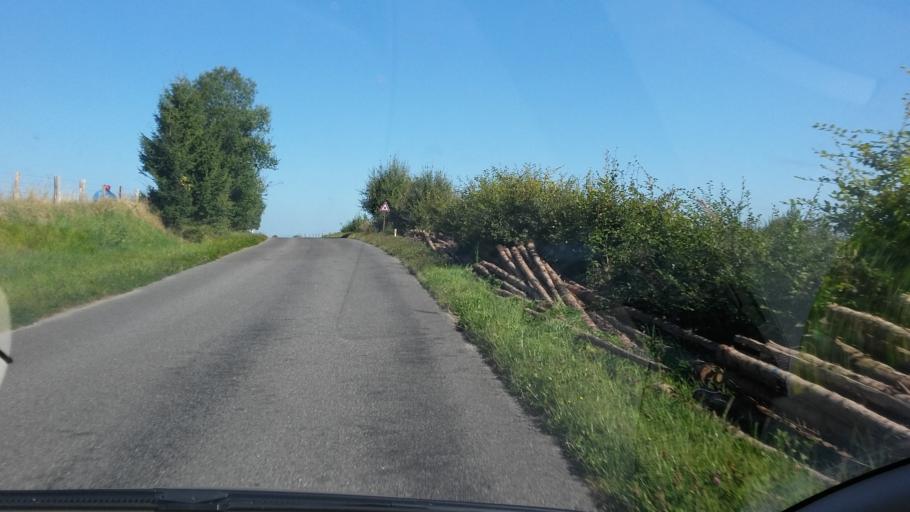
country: BE
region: Wallonia
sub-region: Province du Luxembourg
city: Neufchateau
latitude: 49.8139
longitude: 5.4152
